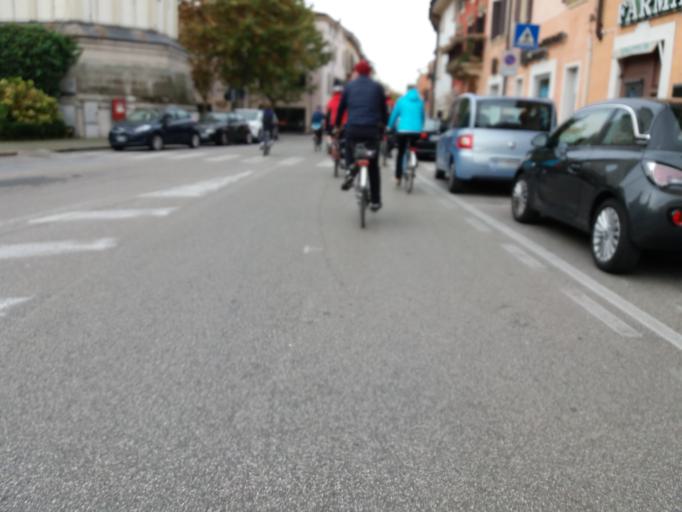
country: IT
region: Veneto
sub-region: Provincia di Verona
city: Bussolengo
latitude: 45.4749
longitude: 10.8471
